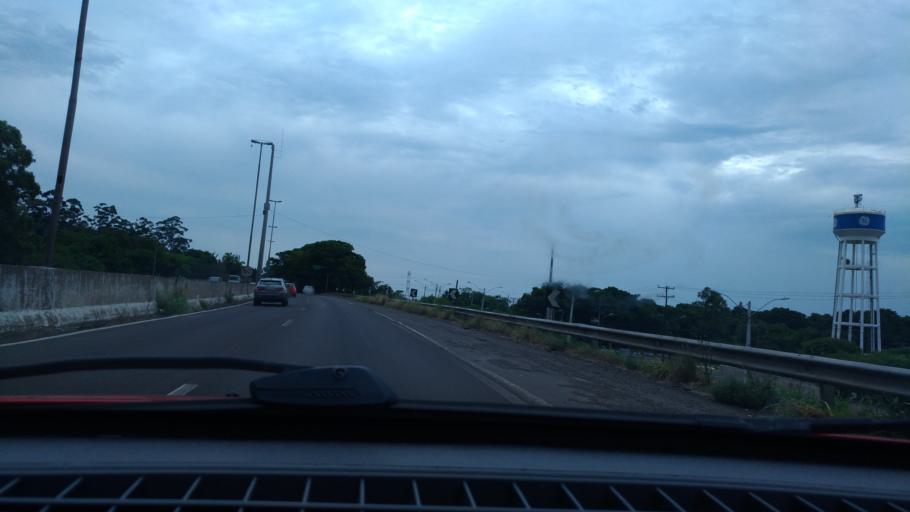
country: BR
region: Rio Grande do Sul
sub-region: Esteio
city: Esteio
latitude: -29.8692
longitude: -51.1804
